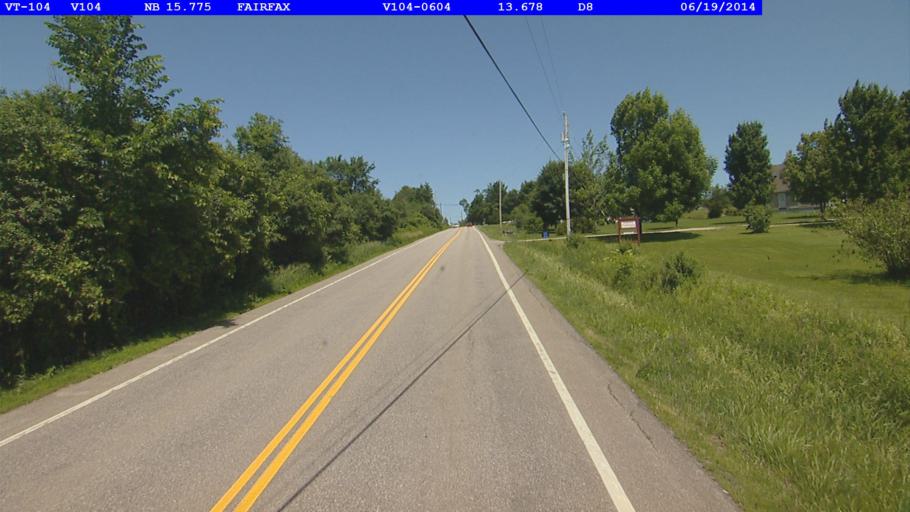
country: US
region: Vermont
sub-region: Franklin County
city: Saint Albans
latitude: 44.7678
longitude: -73.0825
